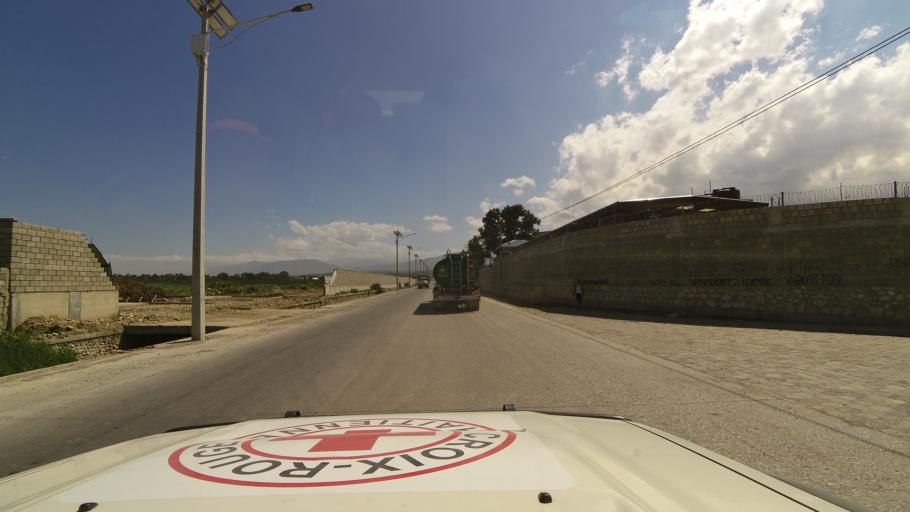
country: HT
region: Ouest
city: Delmas 73
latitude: 18.5884
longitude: -72.3192
